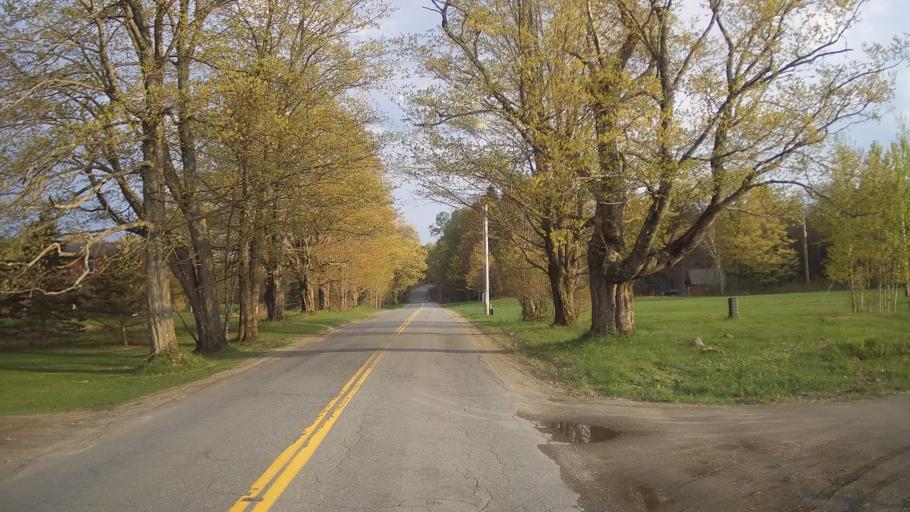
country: US
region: Vermont
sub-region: Orleans County
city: Newport
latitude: 44.9153
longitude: -72.4308
